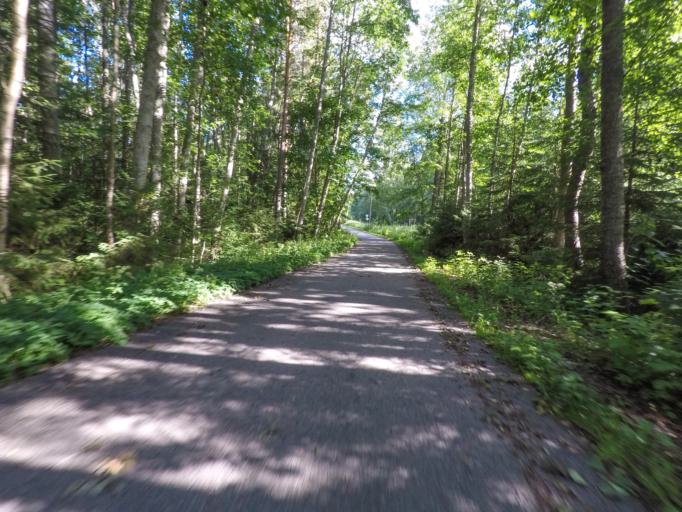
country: FI
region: South Karelia
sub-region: Lappeenranta
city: Lappeenranta
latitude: 61.0859
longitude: 28.1461
